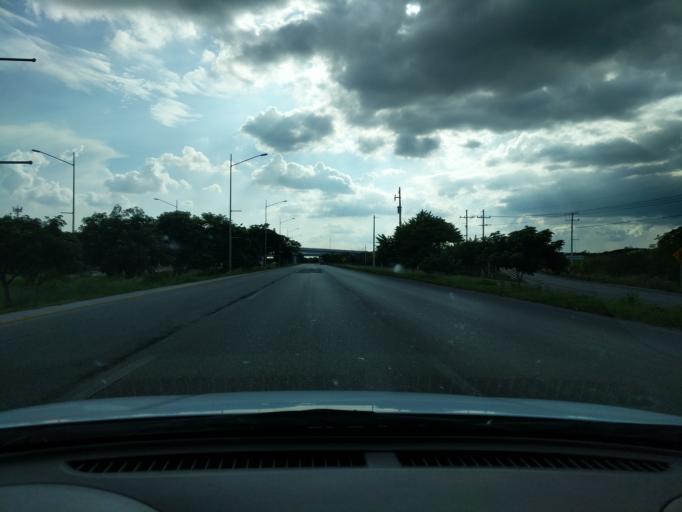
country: MX
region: Yucatan
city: Caucel
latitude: 20.9793
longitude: -89.6848
